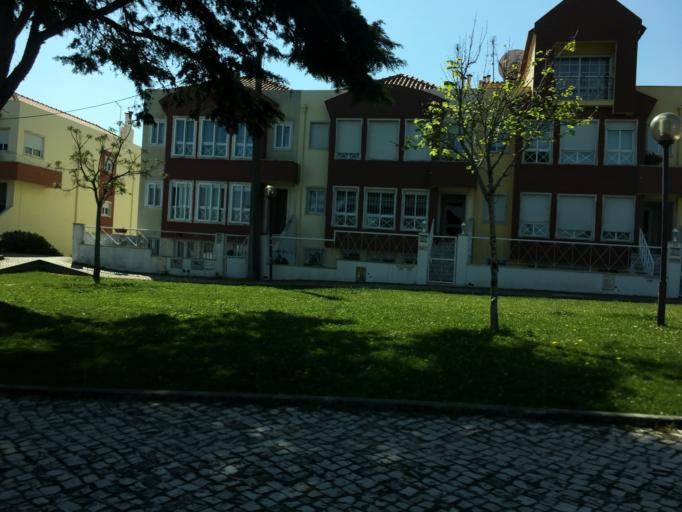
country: PT
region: Lisbon
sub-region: Sintra
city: Sintra
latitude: 38.8071
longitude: -9.3786
